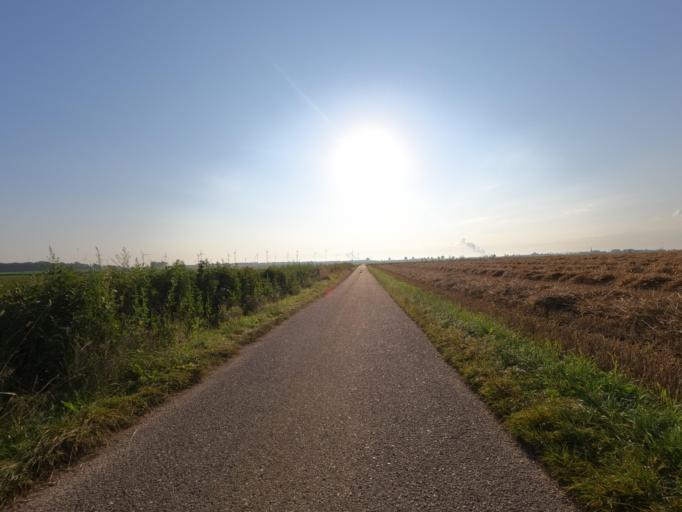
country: DE
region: North Rhine-Westphalia
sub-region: Regierungsbezirk Koln
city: Titz
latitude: 51.0145
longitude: 6.4552
